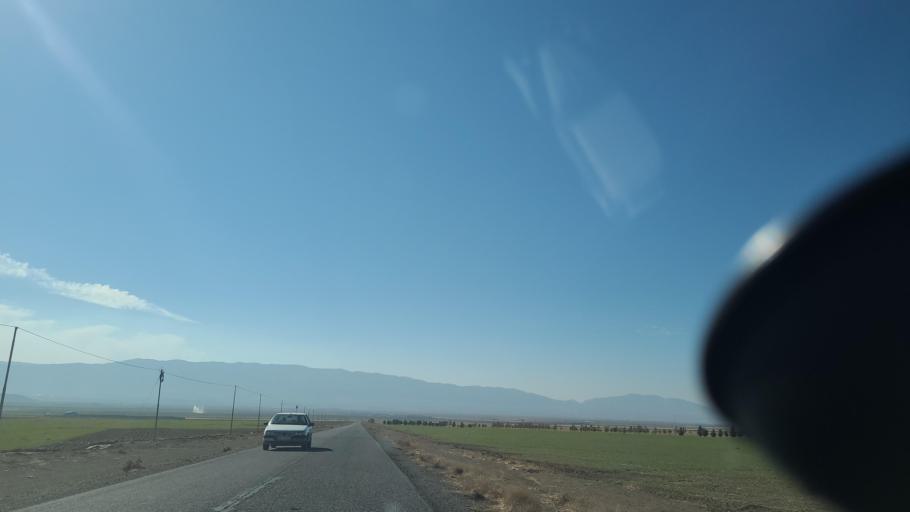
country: IR
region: Razavi Khorasan
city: Dowlatabad
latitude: 35.6081
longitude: 59.4663
